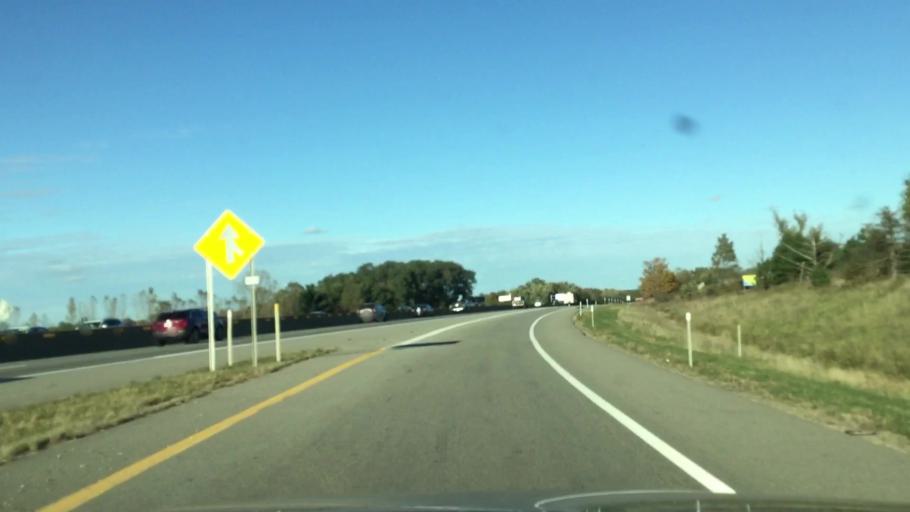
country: US
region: Michigan
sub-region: Kalamazoo County
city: Eastwood
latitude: 42.2604
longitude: -85.5290
